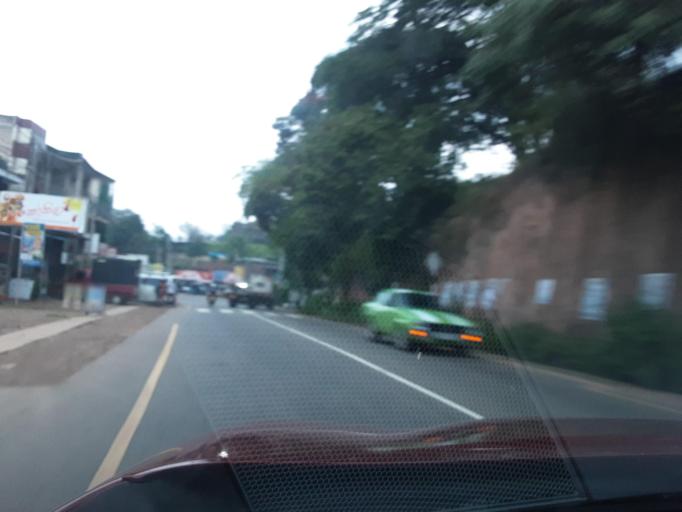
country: LK
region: Central
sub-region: Nuwara Eliya District
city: Nuwara Eliya
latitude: 6.9022
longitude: 80.9013
